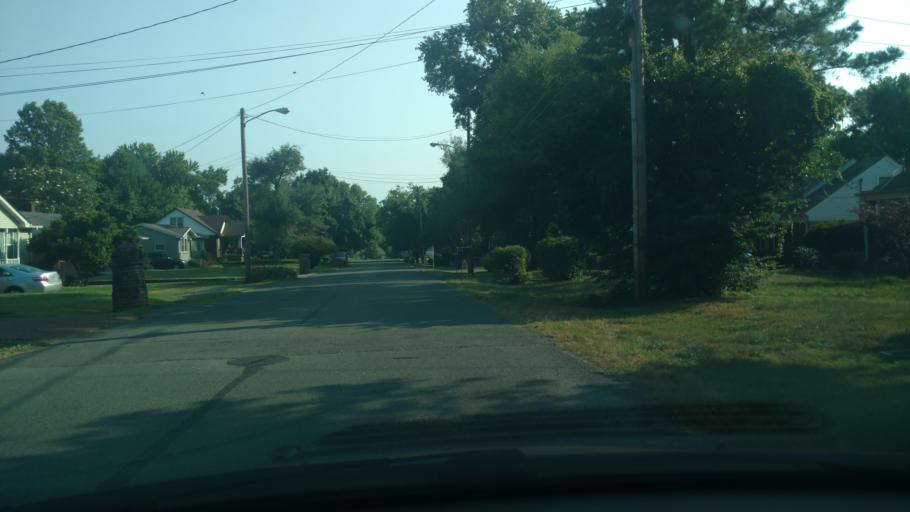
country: US
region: Tennessee
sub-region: Davidson County
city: Lakewood
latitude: 36.2127
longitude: -86.7102
